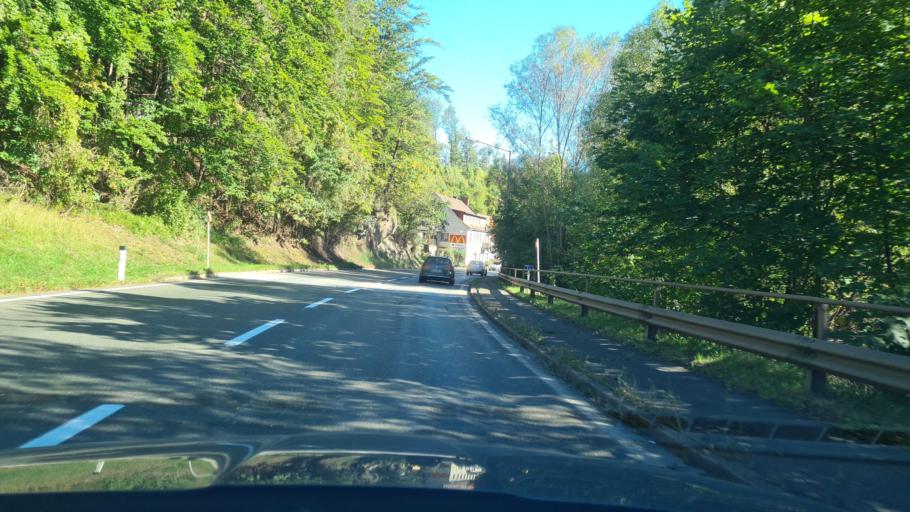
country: AT
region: Styria
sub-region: Politischer Bezirk Leoben
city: Leoben
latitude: 47.3790
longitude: 15.0784
